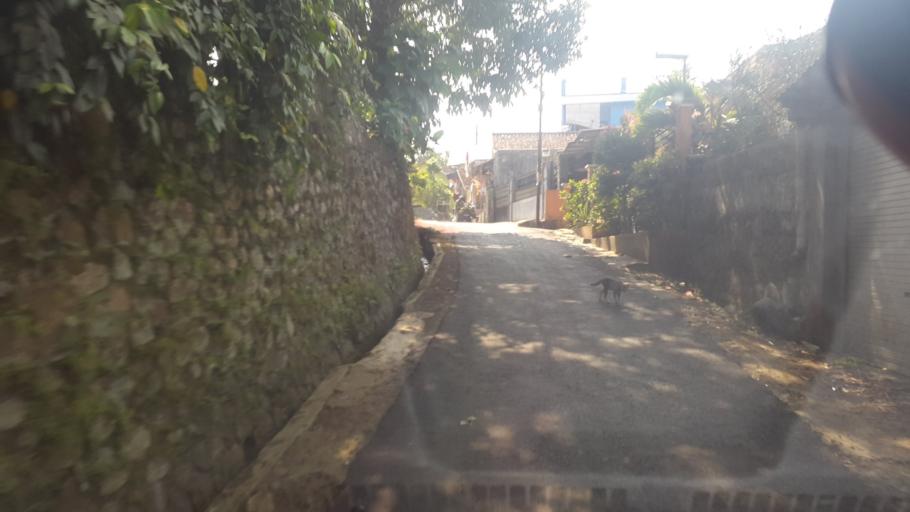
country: ID
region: West Java
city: Gunungkalong
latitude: -6.8917
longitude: 106.7840
